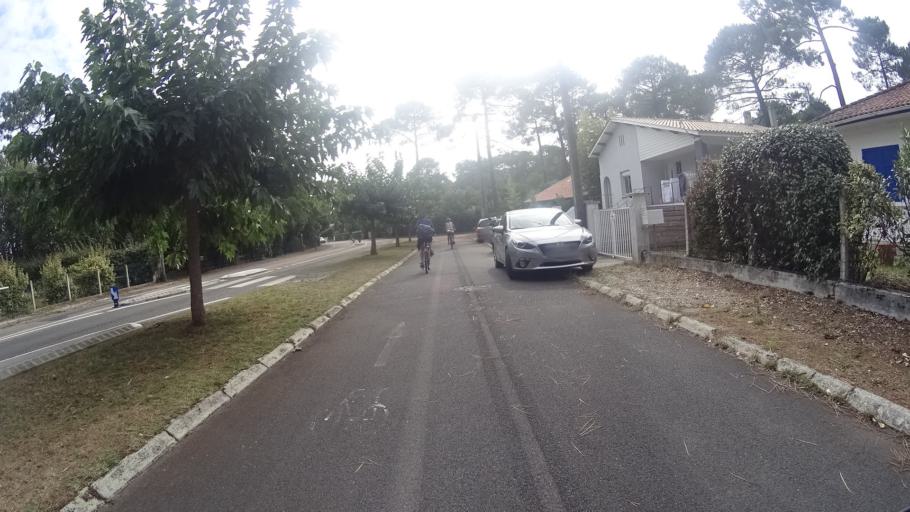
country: FR
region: Aquitaine
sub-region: Departement de la Gironde
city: Lacanau
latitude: 44.9950
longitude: -1.1451
